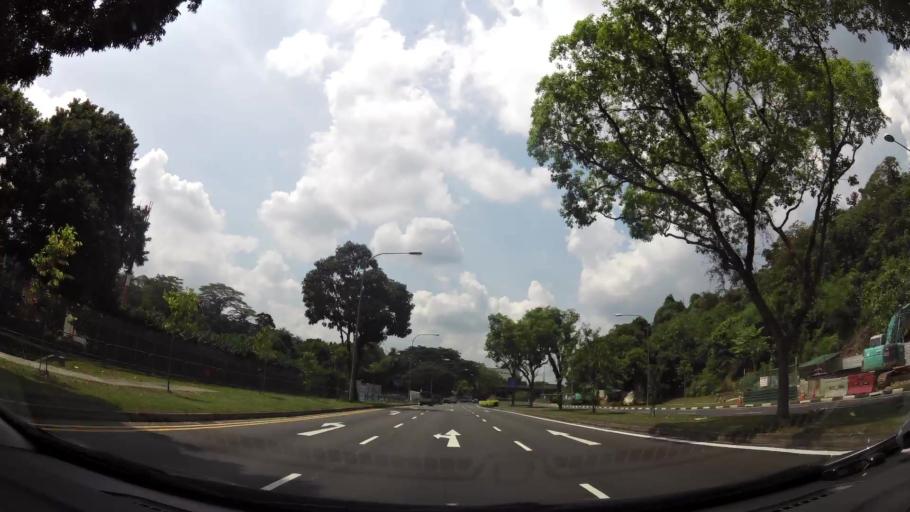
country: MY
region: Johor
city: Johor Bahru
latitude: 1.4101
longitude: 103.7740
